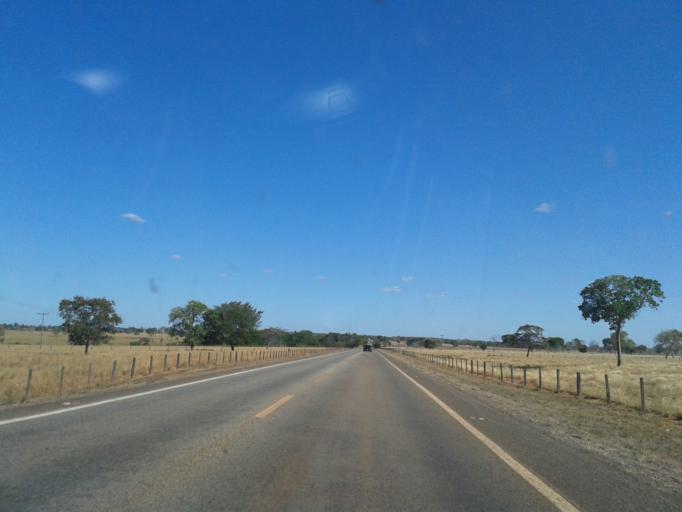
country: BR
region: Goias
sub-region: Mozarlandia
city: Mozarlandia
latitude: -14.2665
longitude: -50.3991
